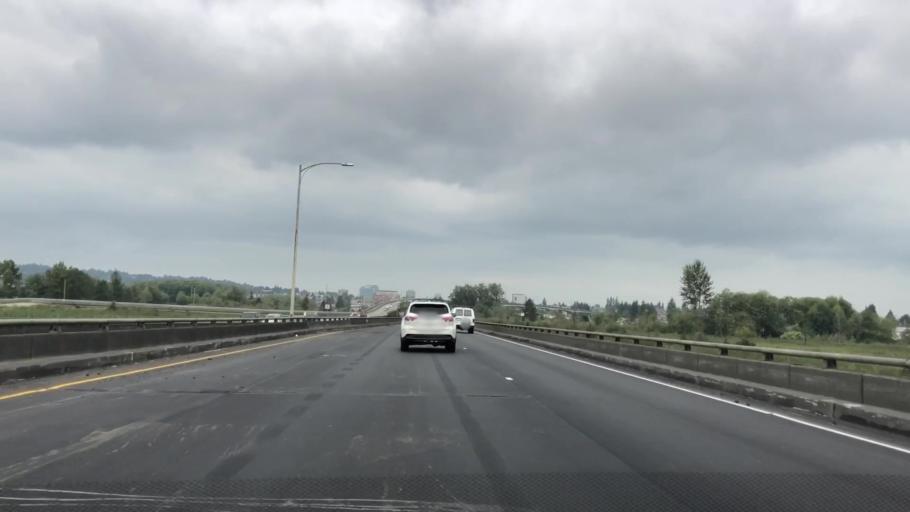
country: US
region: Washington
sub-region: Snohomish County
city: Everett
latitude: 47.9773
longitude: -122.1716
